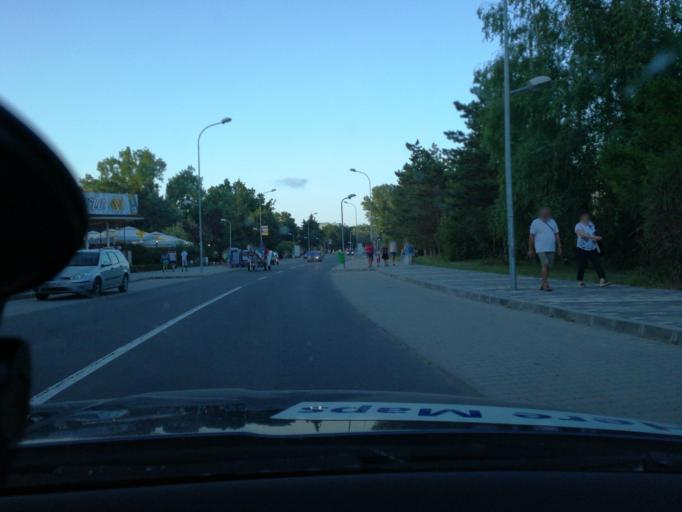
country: RO
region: Constanta
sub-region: Comuna Douazeci si Trei August
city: Douazeci si Trei August
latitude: 43.8712
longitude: 28.5981
